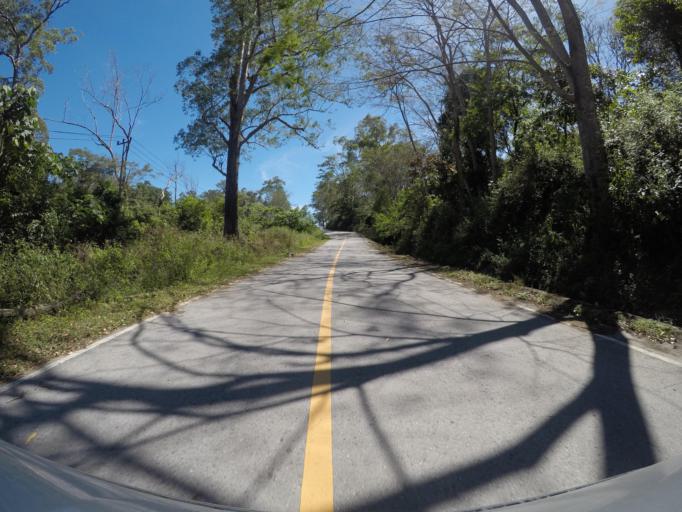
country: TL
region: Manufahi
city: Same
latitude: -8.8959
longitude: 125.9824
